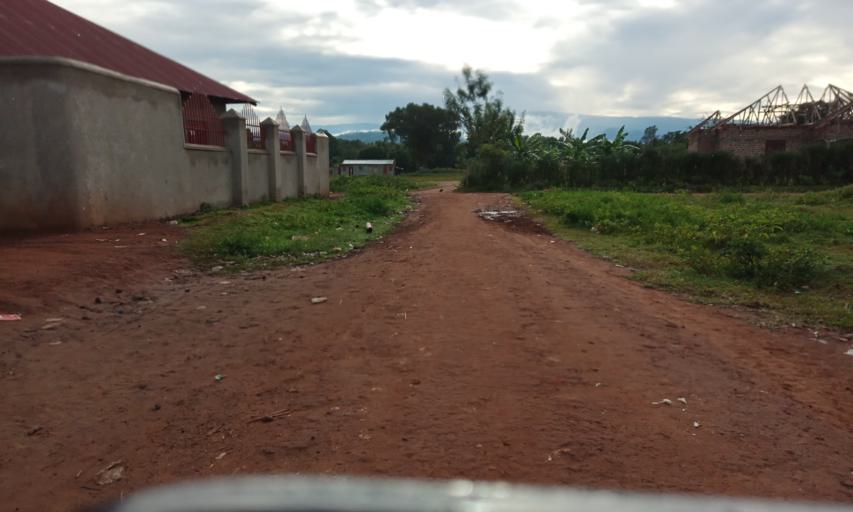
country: UG
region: Eastern Region
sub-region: Mbale District
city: Mbale
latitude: 1.1443
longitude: 34.1670
